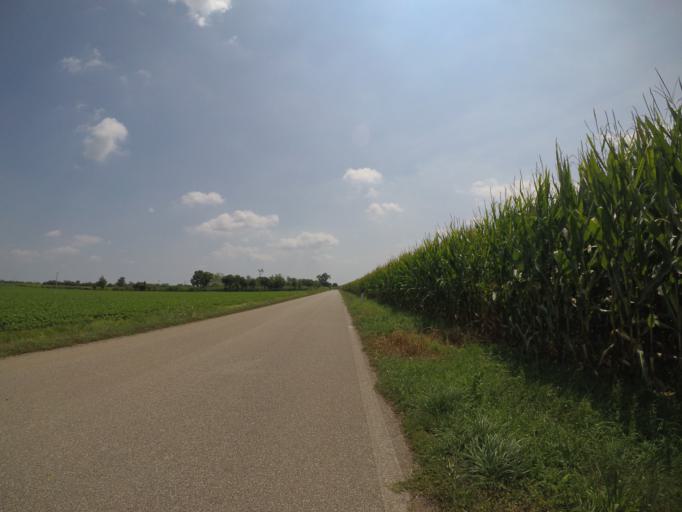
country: IT
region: Friuli Venezia Giulia
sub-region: Provincia di Udine
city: Bertiolo
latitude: 45.9687
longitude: 13.0720
